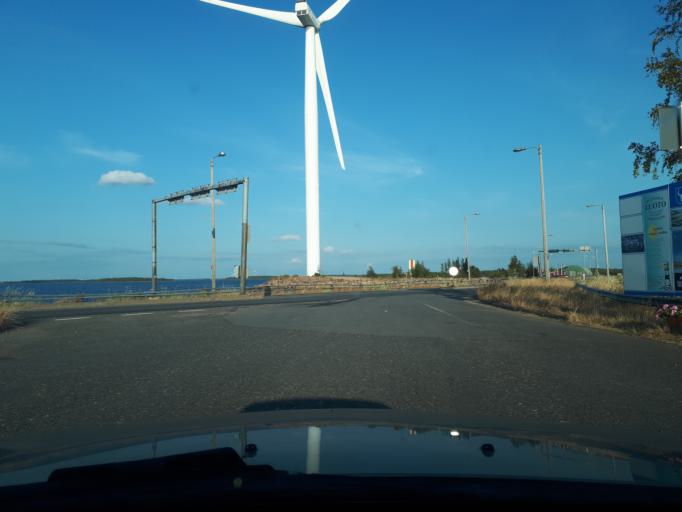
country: FI
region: Northern Ostrobothnia
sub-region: Oulu
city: Lumijoki
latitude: 65.0085
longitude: 25.1970
